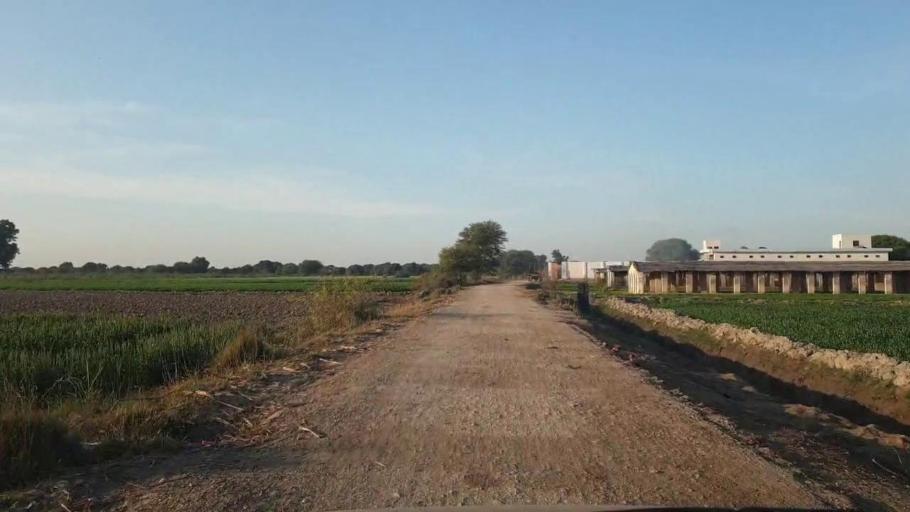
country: PK
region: Sindh
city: Chambar
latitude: 25.2712
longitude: 68.7728
